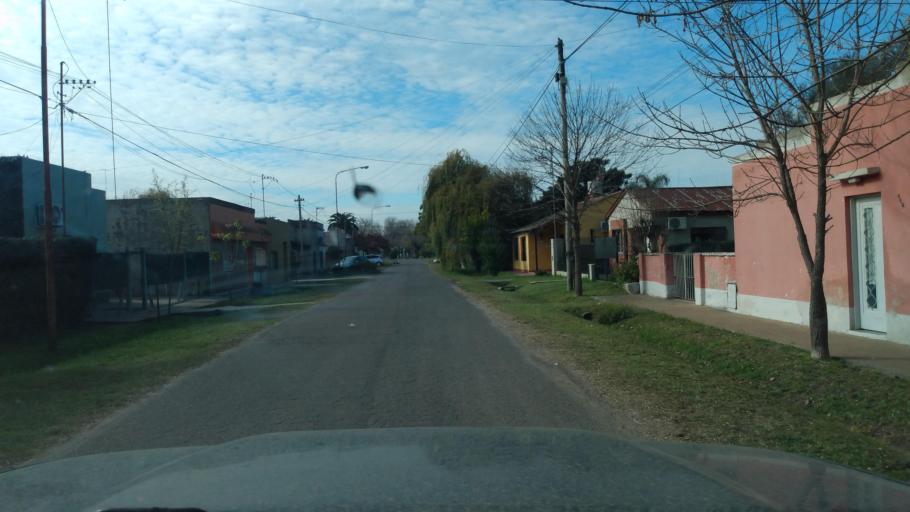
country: AR
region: Buenos Aires
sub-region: Partido de Lujan
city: Lujan
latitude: -34.5964
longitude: -59.1789
